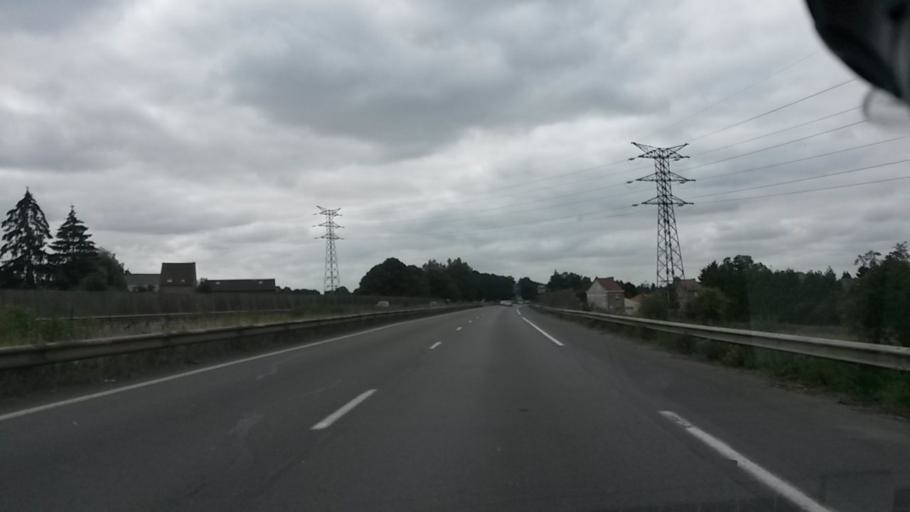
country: FR
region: Nord-Pas-de-Calais
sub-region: Departement du Nord
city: Haulchin
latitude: 50.3198
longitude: 3.4219
